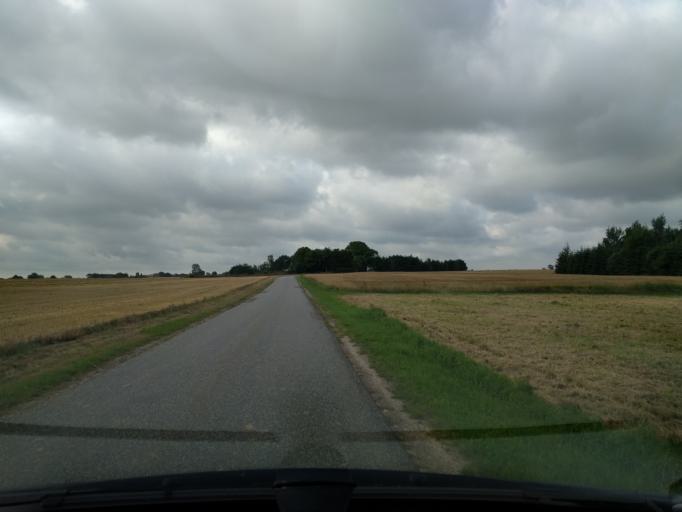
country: DK
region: Zealand
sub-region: Guldborgsund Kommune
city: Stubbekobing
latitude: 54.9036
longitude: 11.9849
